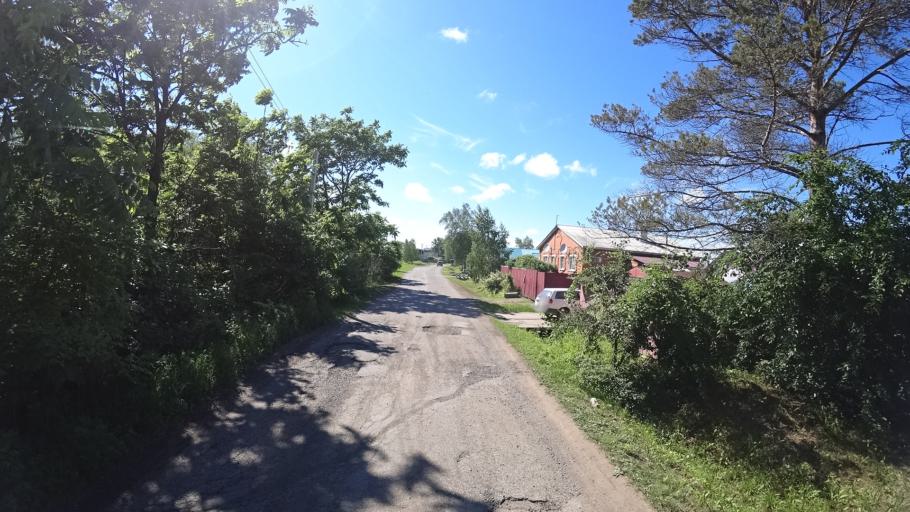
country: RU
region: Khabarovsk Krai
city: Khor
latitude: 47.8859
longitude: 134.9960
